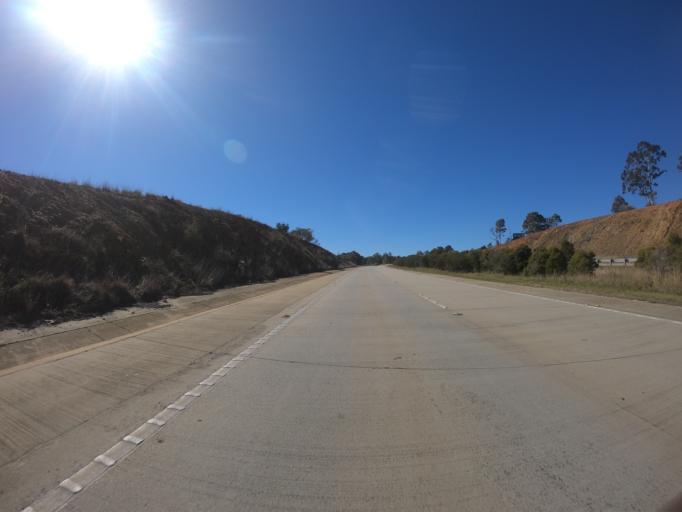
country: AU
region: New South Wales
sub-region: Yass Valley
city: Gundaroo
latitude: -35.1186
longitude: 149.3490
